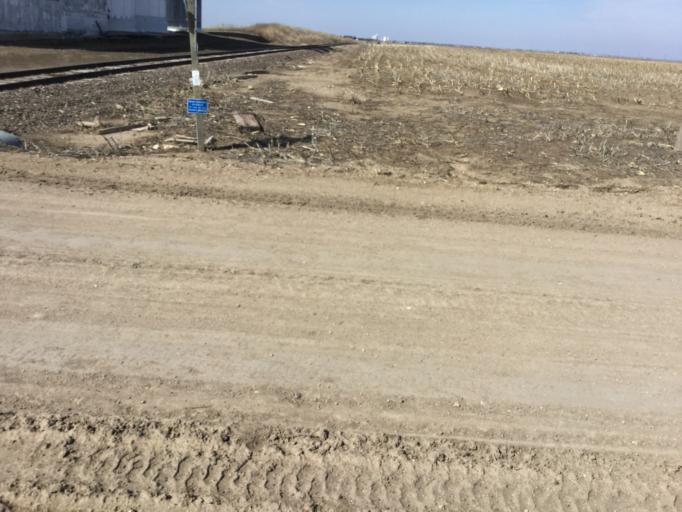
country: US
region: Kansas
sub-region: Scott County
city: Scott City
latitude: 38.4869
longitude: -100.8331
